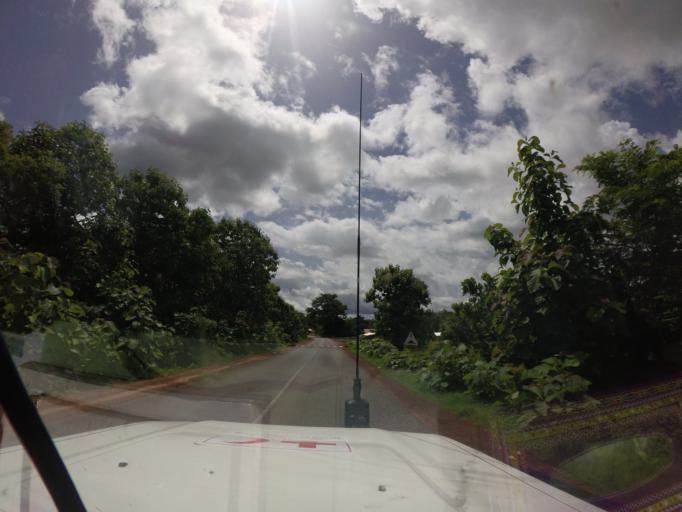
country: SL
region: Northern Province
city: Bindi
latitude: 10.1771
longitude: -11.7190
